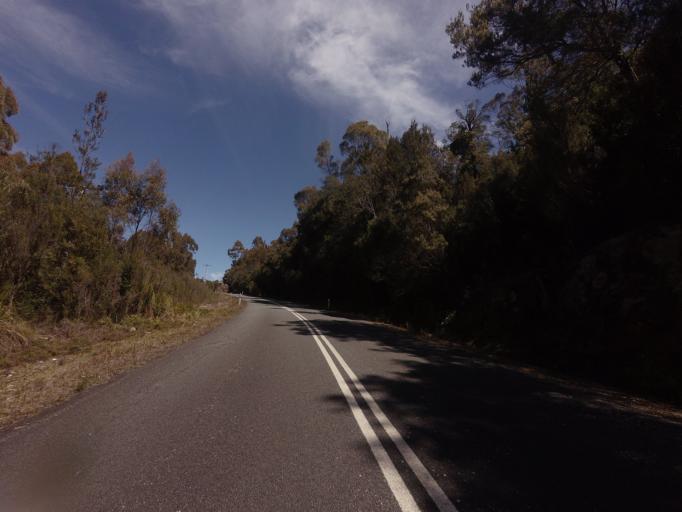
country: AU
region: Tasmania
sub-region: West Coast
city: Queenstown
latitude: -42.7807
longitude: 146.0340
